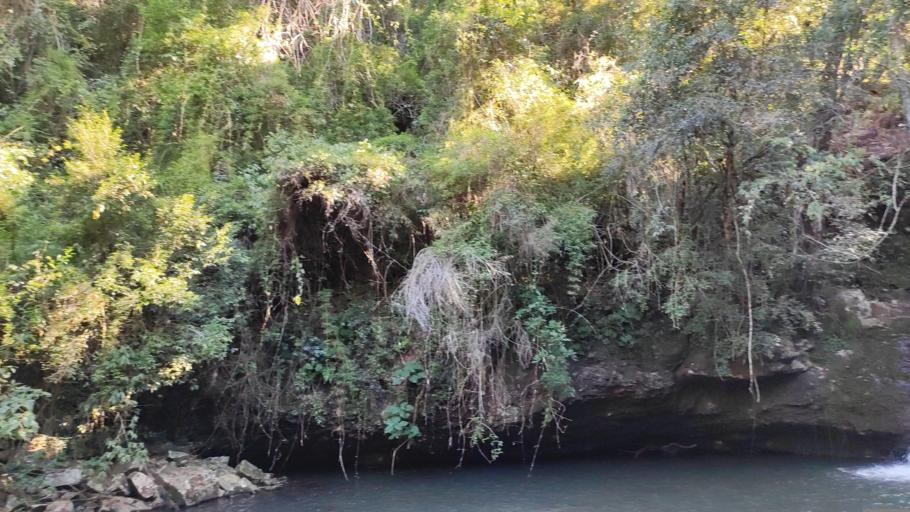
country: AR
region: Misiones
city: Dos de Mayo
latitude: -26.9925
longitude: -54.6300
